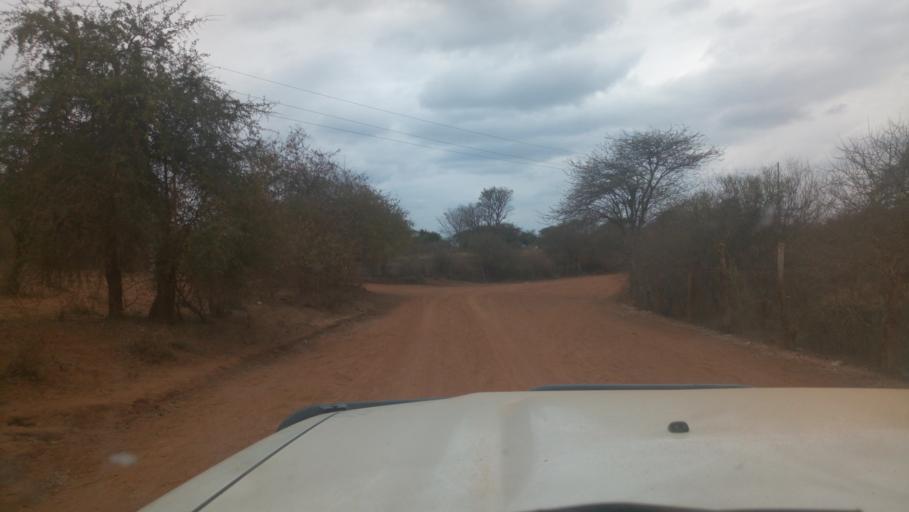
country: KE
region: Makueni
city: Wote
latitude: -1.6284
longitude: 37.8731
